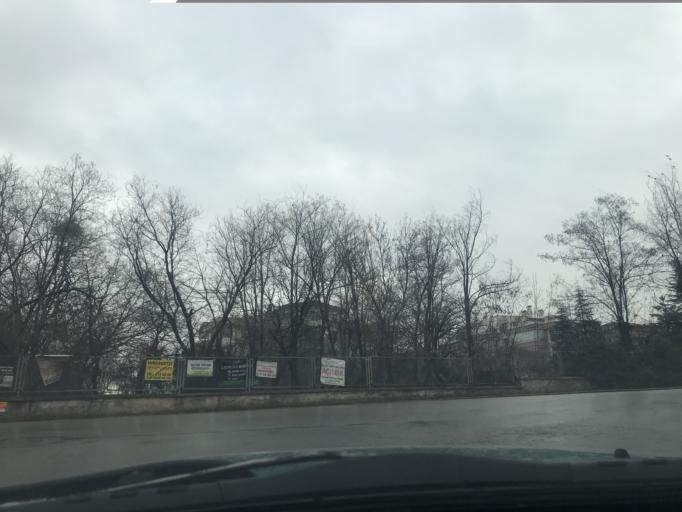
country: TR
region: Ankara
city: Batikent
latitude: 39.9130
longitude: 32.7700
